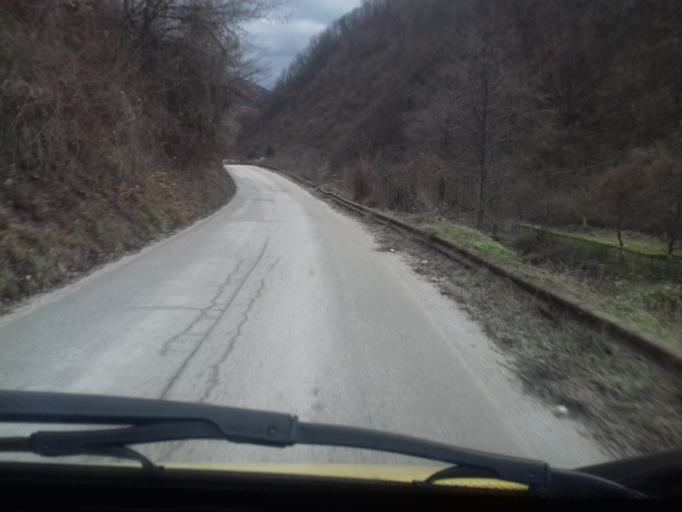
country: BA
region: Federation of Bosnia and Herzegovina
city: Zenica
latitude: 44.2307
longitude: 17.9864
